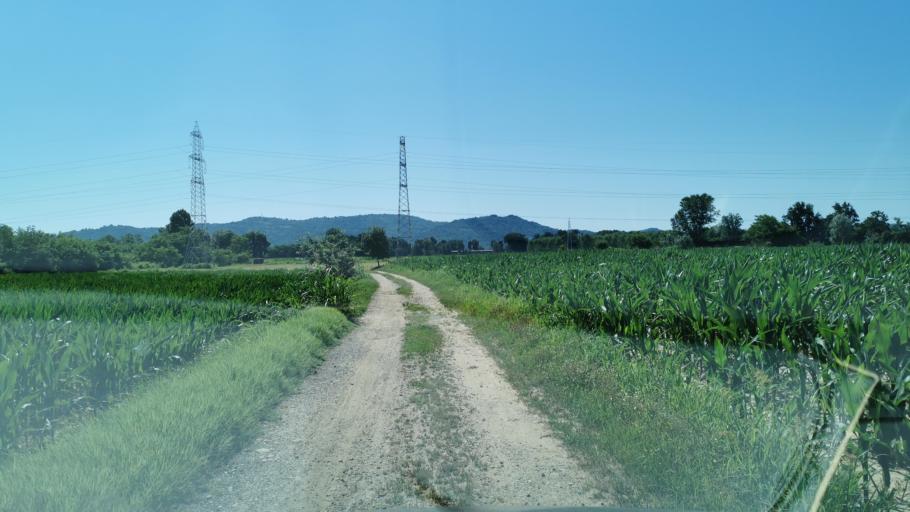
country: IT
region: Piedmont
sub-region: Provincia di Torino
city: Brandizzo
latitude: 45.1935
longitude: 7.8308
